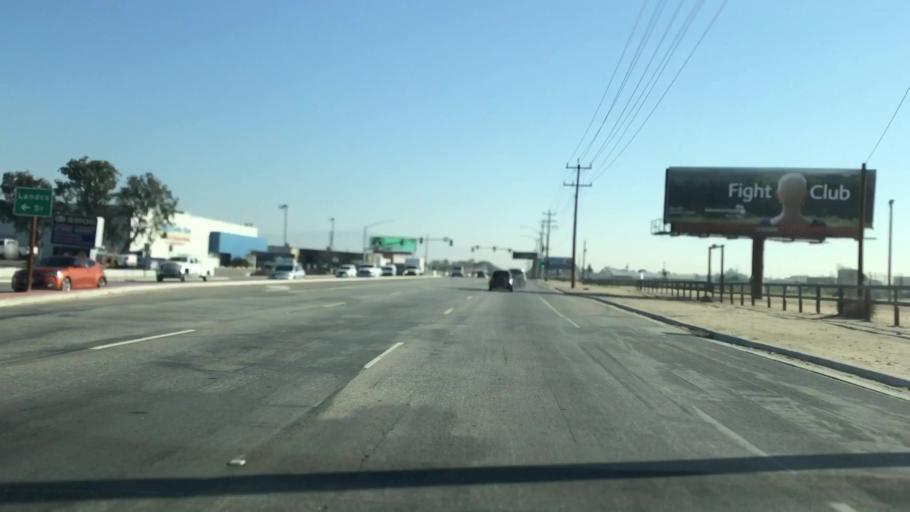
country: US
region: California
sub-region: Kern County
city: Bakersfield
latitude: 35.3832
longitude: -119.0611
